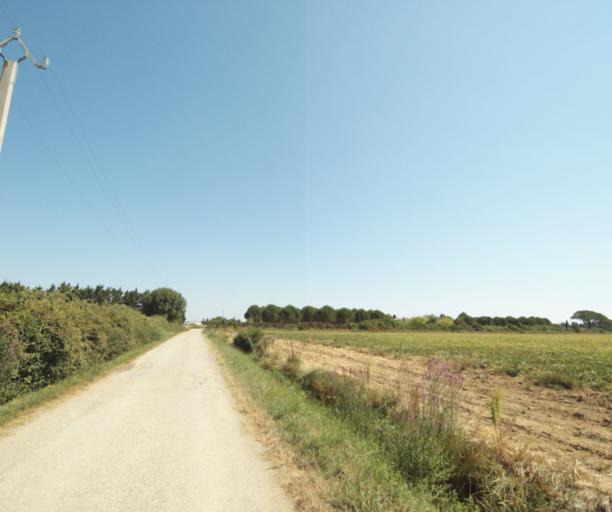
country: FR
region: Languedoc-Roussillon
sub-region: Departement de l'Herault
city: Marsillargues
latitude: 43.6440
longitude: 4.1609
